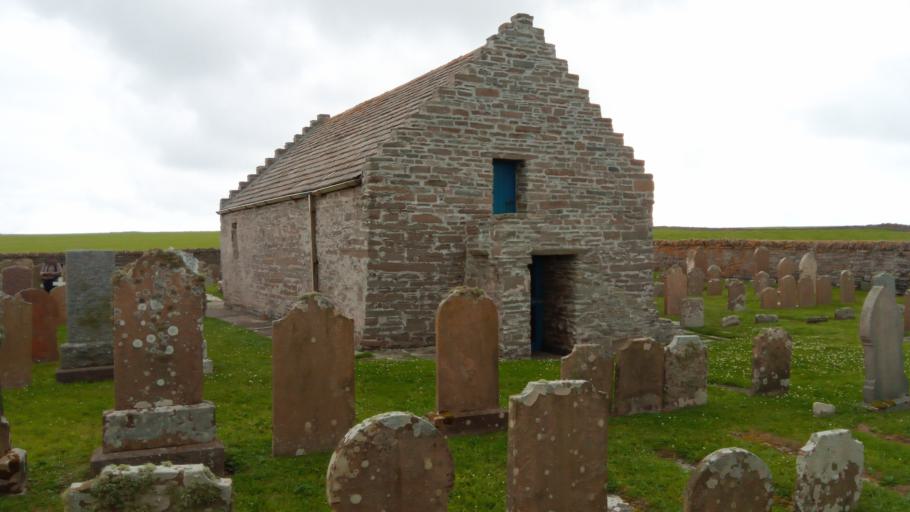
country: GB
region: Scotland
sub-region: Orkney Islands
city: Kirkwall
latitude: 59.3577
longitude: -2.9017
